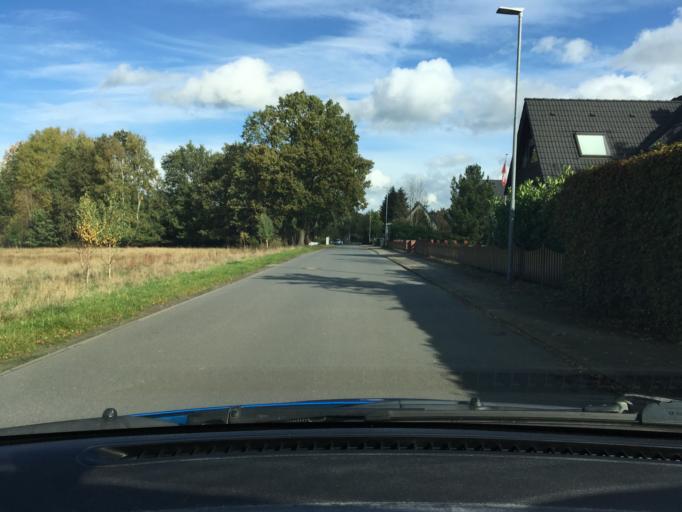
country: DE
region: Lower Saxony
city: Kakenstorf
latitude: 53.3159
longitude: 9.7906
